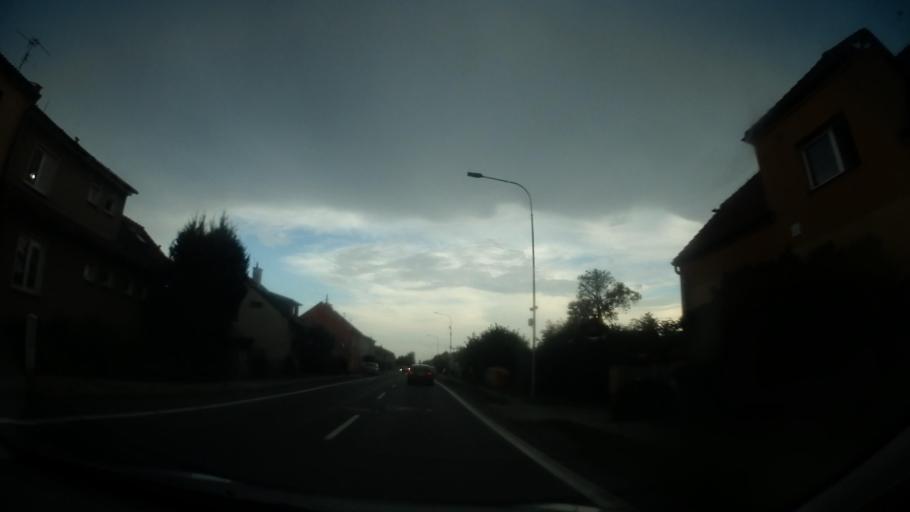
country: CZ
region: Olomoucky
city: Horka nad Moravou
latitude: 49.6371
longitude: 17.2329
